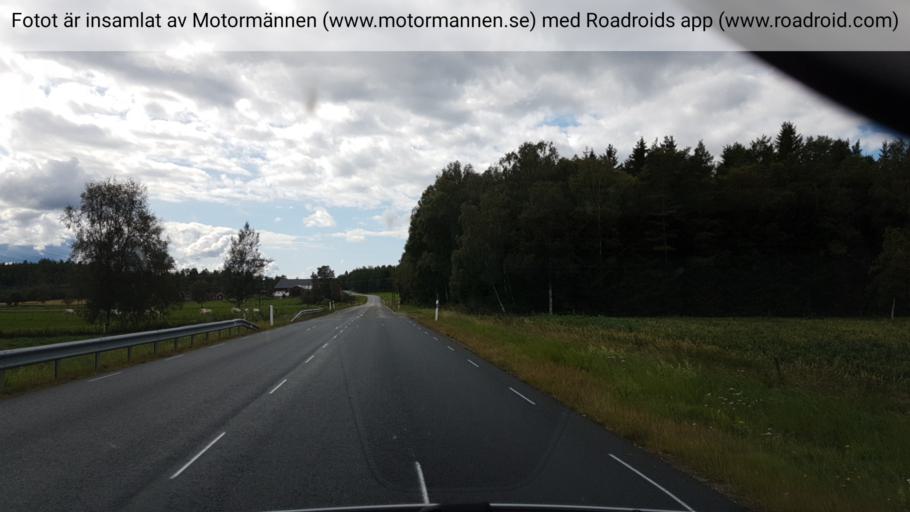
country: SE
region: Joenkoeping
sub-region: Aneby Kommun
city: Aneby
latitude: 57.9805
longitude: 14.8240
